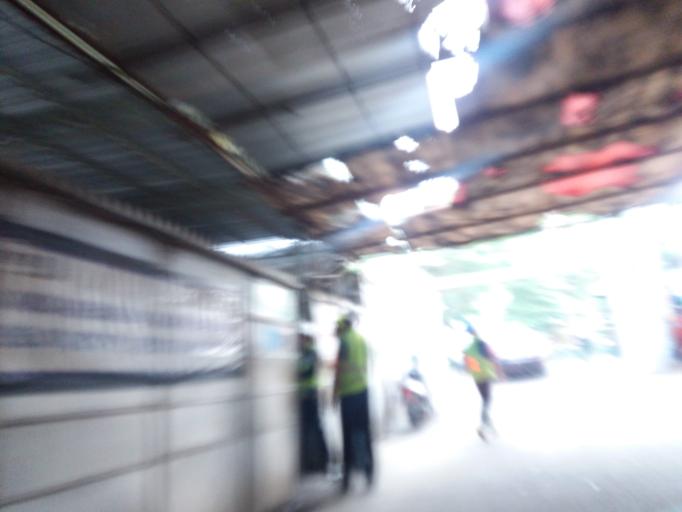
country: ID
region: Jakarta Raya
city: Jakarta
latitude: -6.2128
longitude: 106.8218
